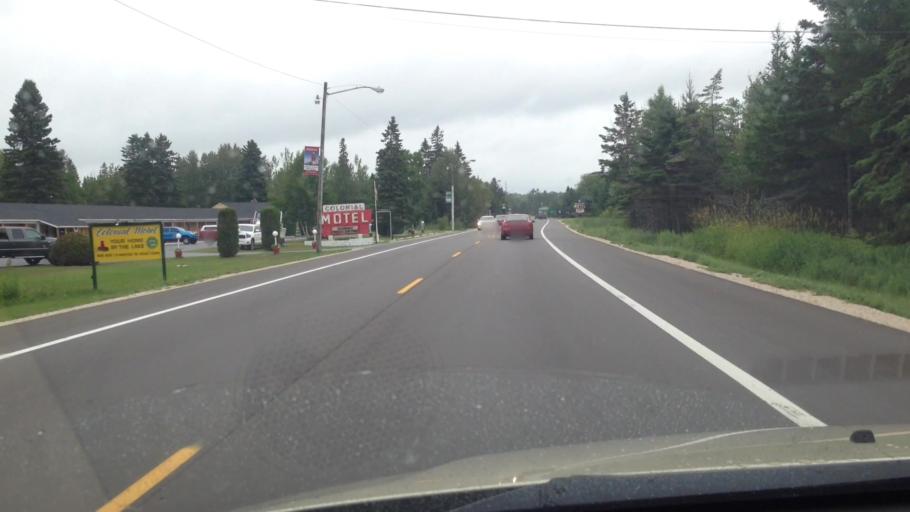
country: US
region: Michigan
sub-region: Schoolcraft County
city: Manistique
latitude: 45.9548
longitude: -86.2259
